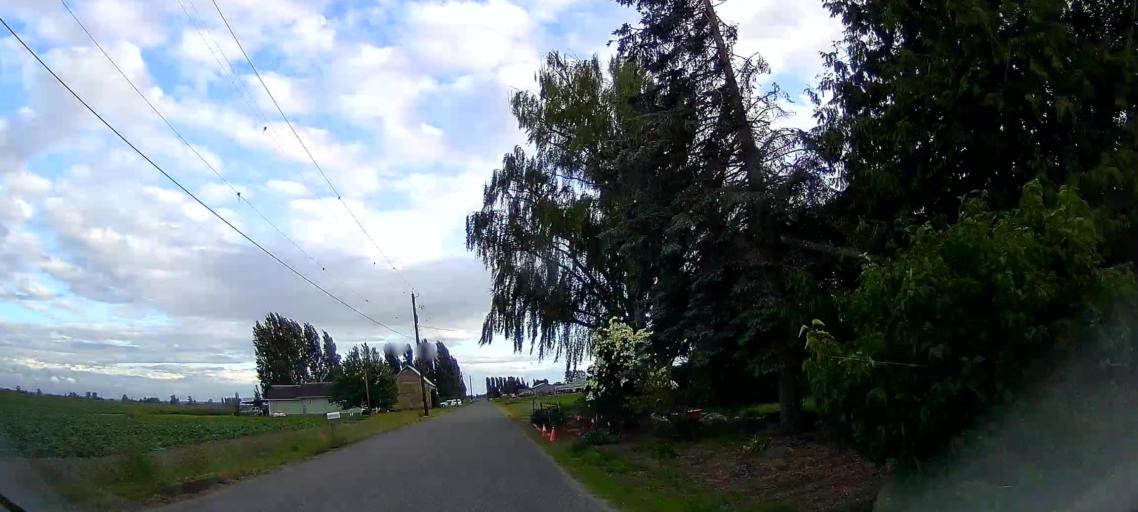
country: US
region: Washington
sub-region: Skagit County
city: Mount Vernon
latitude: 48.3790
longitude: -122.4004
